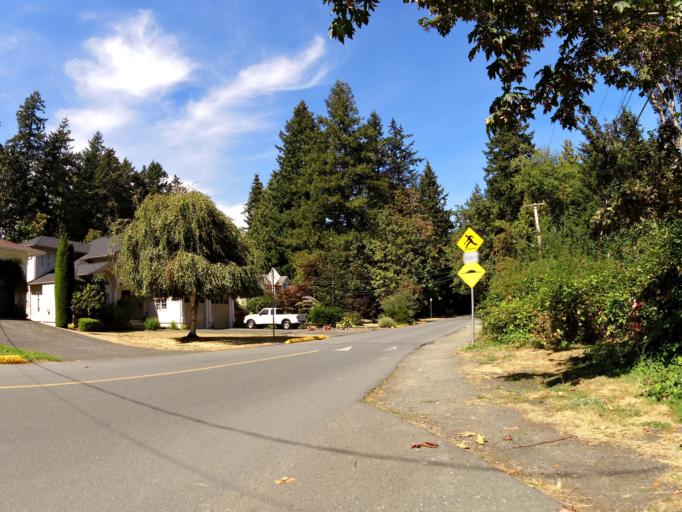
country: CA
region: British Columbia
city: Victoria
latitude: 48.5322
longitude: -123.3756
